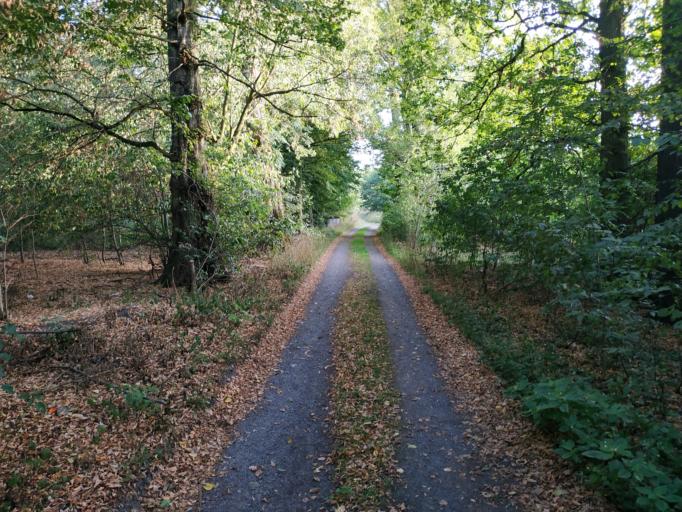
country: PL
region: Lower Silesian Voivodeship
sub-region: Powiat zgorzelecki
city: Lagow
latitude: 51.1934
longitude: 15.1020
